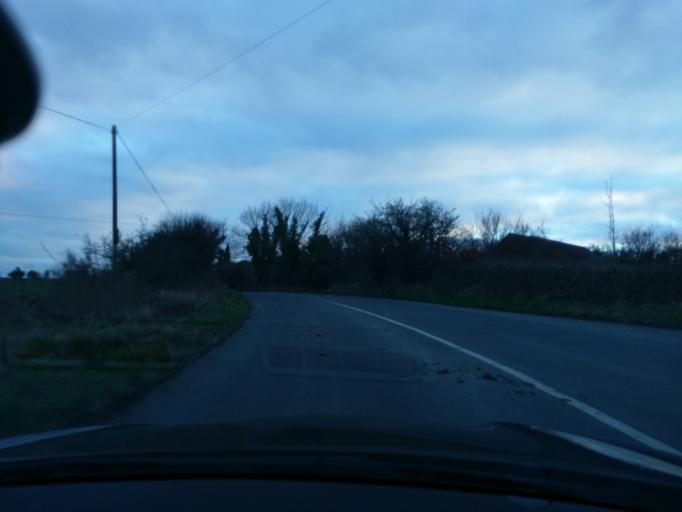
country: IE
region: Connaught
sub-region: County Galway
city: Athenry
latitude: 53.3699
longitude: -8.7750
